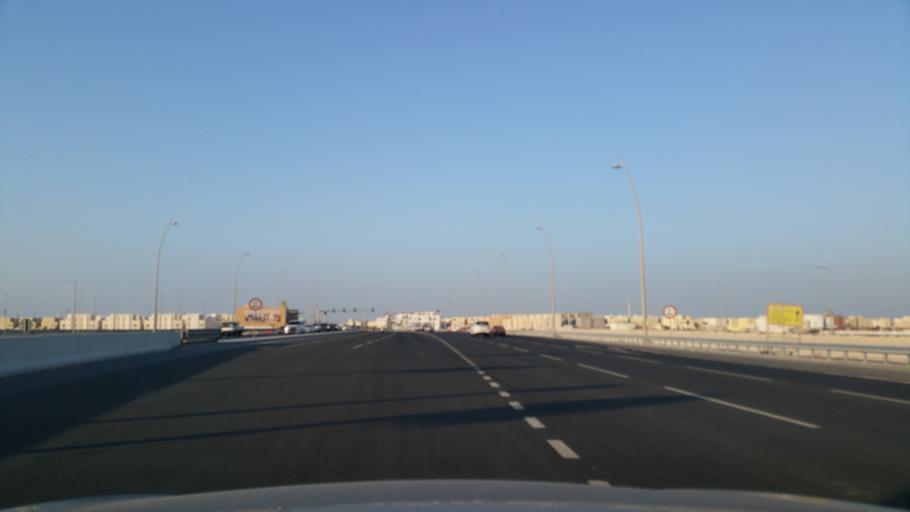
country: QA
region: Al Khawr
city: Al Khawr
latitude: 25.6610
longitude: 51.5006
